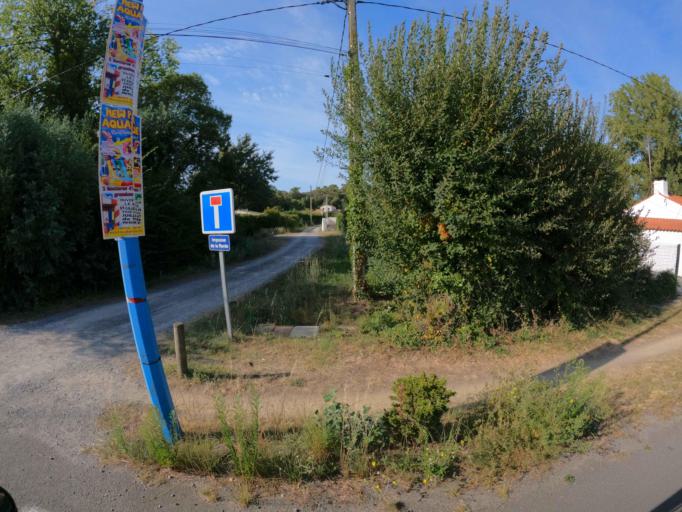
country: FR
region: Pays de la Loire
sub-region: Departement de la Vendee
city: Saint-Jean-de-Monts
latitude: 46.8075
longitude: -2.1025
